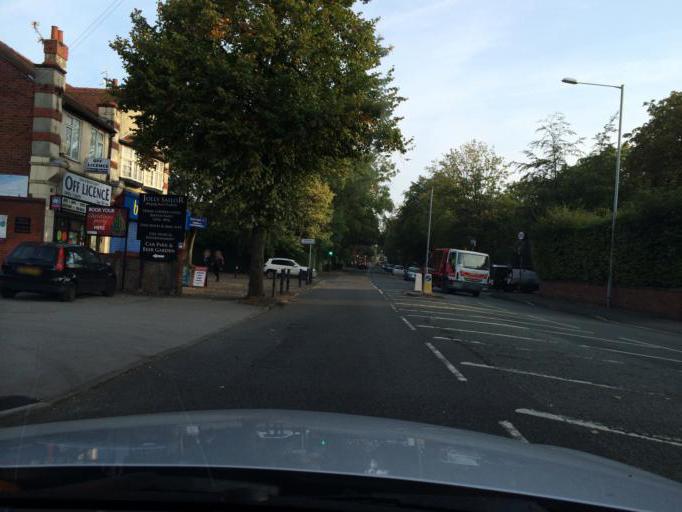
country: GB
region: England
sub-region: Borough of Stockport
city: Stockport
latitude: 53.3855
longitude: -2.1532
